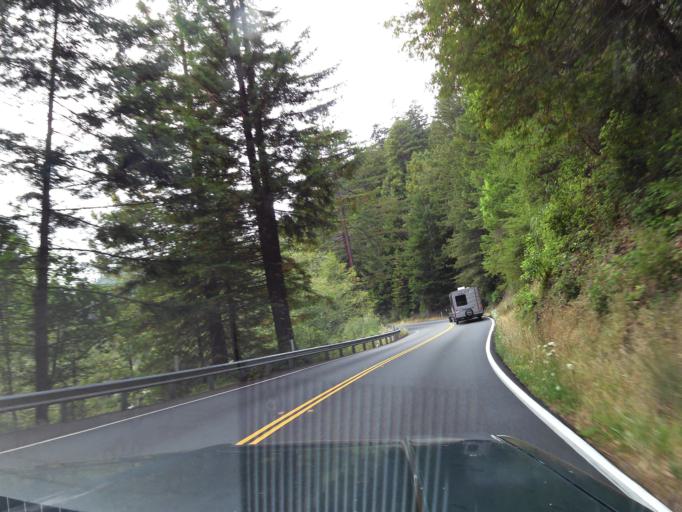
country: US
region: California
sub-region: Mendocino County
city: Fort Bragg
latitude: 39.1790
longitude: -123.6940
